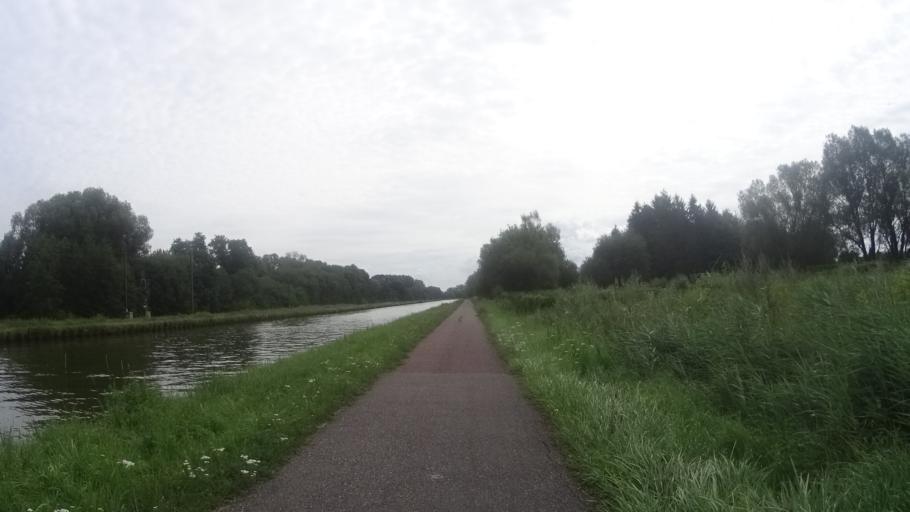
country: FR
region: Alsace
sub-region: Departement du Bas-Rhin
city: Steinbourg
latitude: 48.7633
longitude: 7.4205
